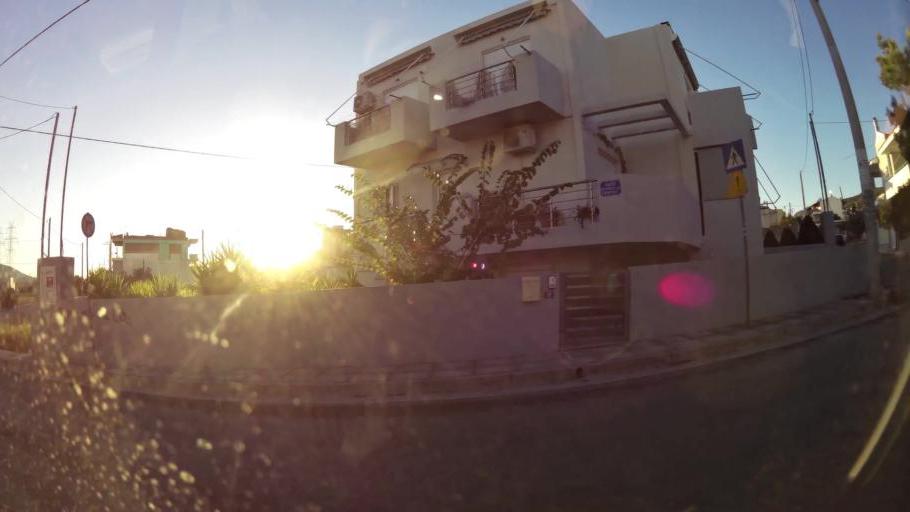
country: GR
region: Attica
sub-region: Nomarchia Dytikis Attikis
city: Ano Liosia
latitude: 38.0933
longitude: 23.7002
